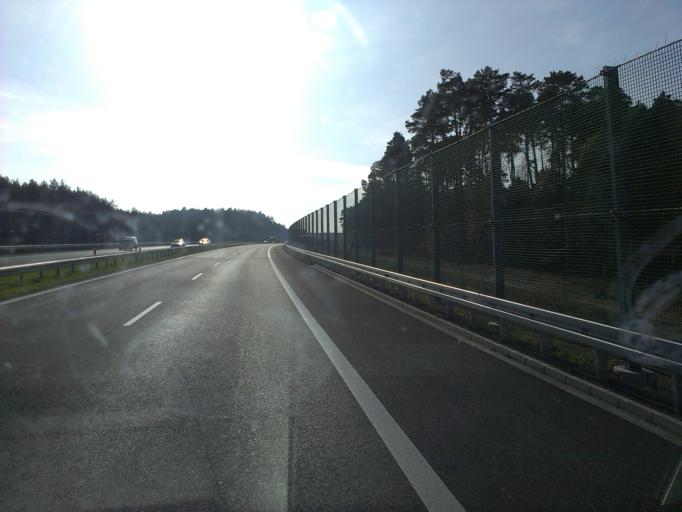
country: PL
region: Lubusz
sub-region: Powiat miedzyrzecki
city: Miedzyrzecz
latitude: 52.5005
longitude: 15.5543
